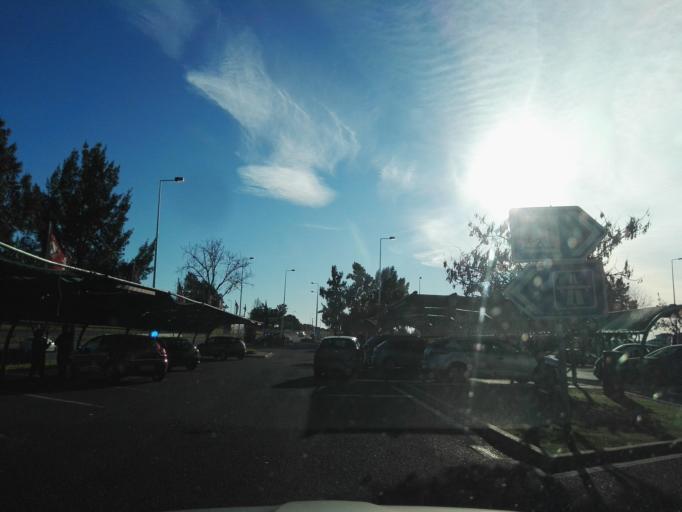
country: PT
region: Lisbon
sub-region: Azambuja
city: Aveiras de Cima
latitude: 39.1238
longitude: -8.9074
